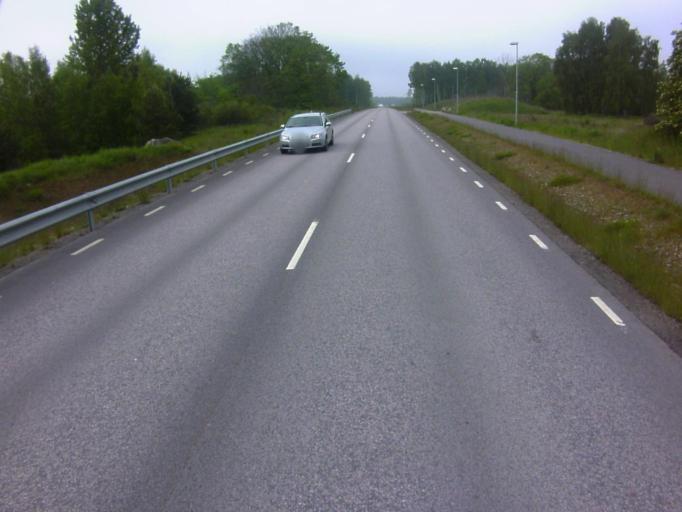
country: SE
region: Blekinge
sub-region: Solvesborgs Kommun
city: Soelvesborg
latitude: 56.0544
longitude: 14.6157
